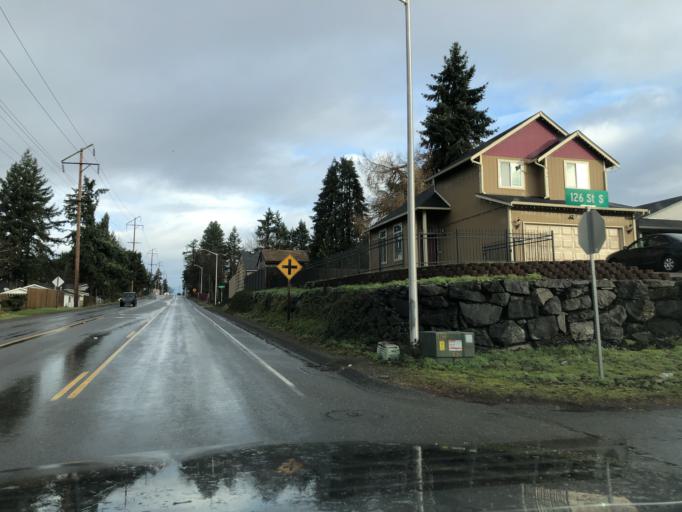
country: US
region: Washington
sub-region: Pierce County
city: Parkland
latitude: 47.1426
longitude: -122.4371
